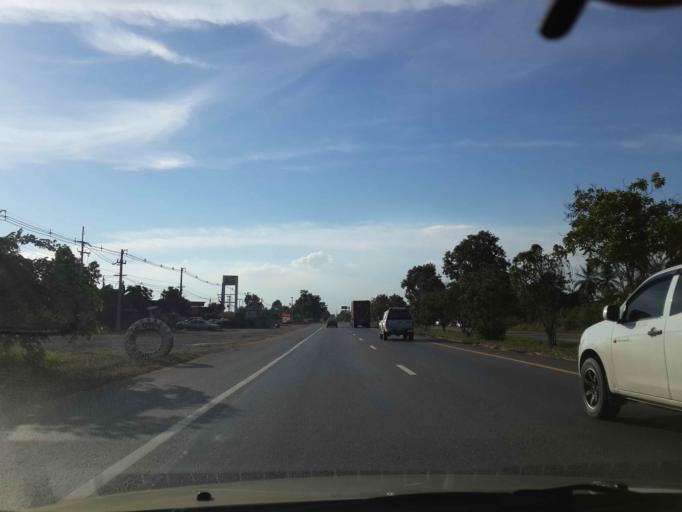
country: TH
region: Chon Buri
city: Phatthaya
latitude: 12.9380
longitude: 100.9968
